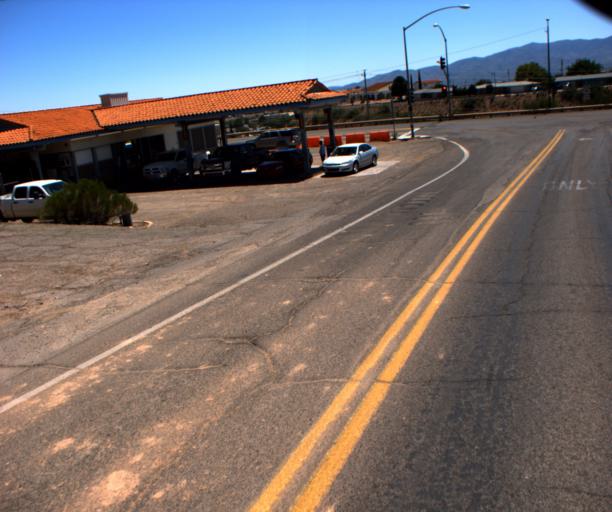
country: US
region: Arizona
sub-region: Greenlee County
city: Clifton
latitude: 33.0512
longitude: -109.3249
